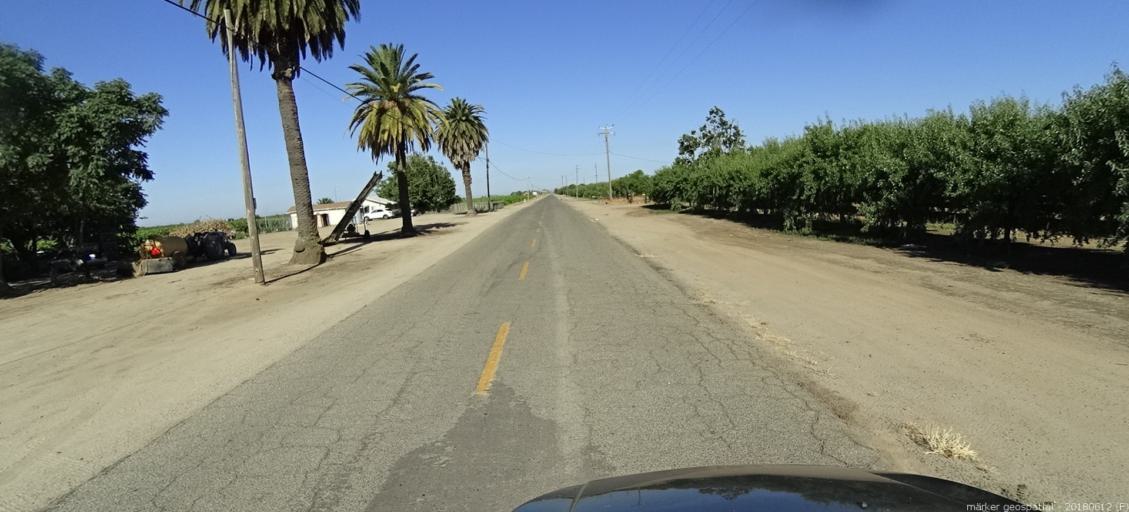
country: US
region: California
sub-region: Madera County
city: Fairmead
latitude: 37.0110
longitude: -120.1517
